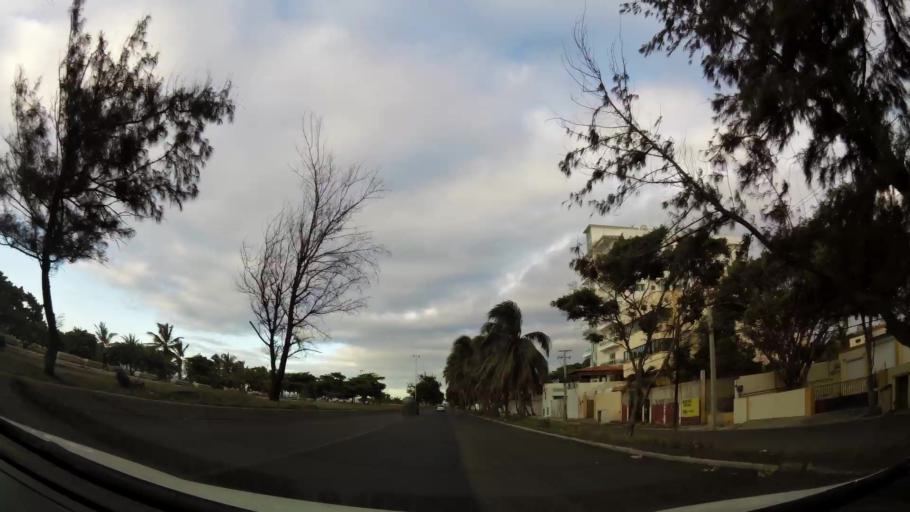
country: DO
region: Nacional
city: Bella Vista
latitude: 18.4299
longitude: -69.9631
